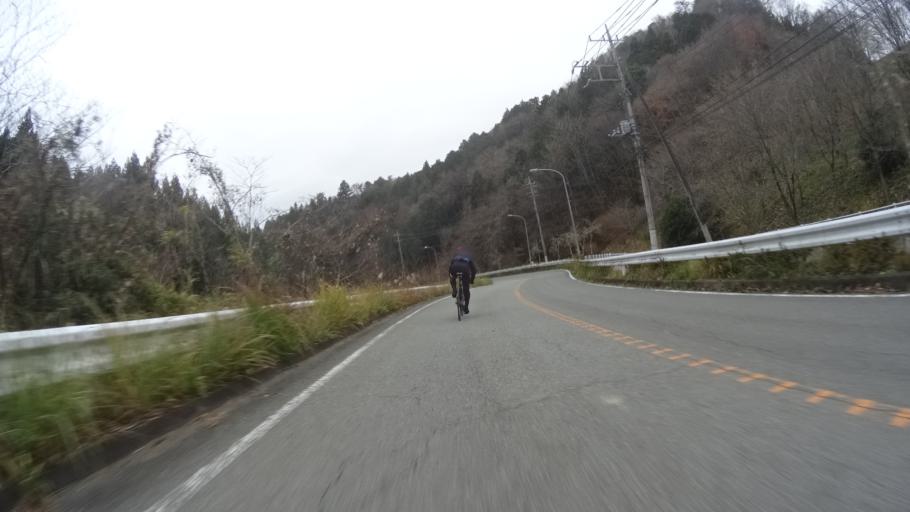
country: JP
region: Yamanashi
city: Uenohara
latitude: 35.6374
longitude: 139.1149
